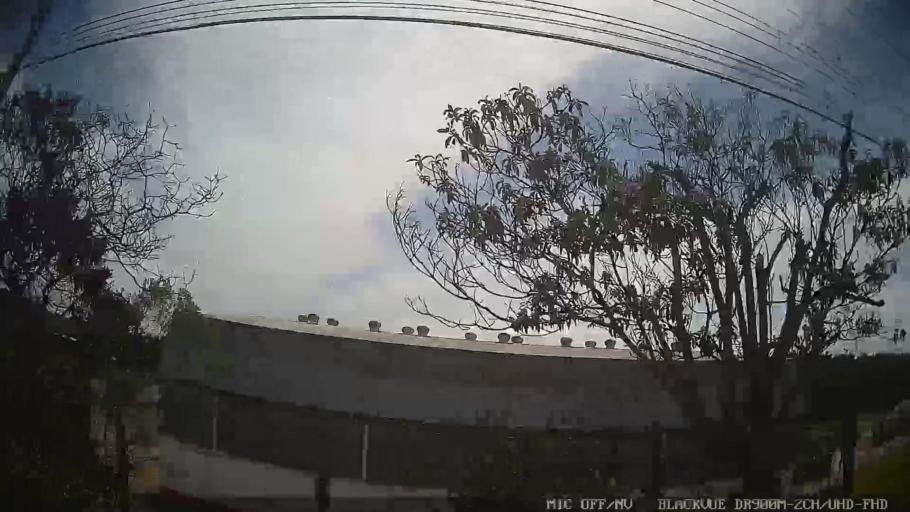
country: BR
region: Sao Paulo
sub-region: Santa Isabel
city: Santa Isabel
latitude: -23.3820
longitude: -46.1773
